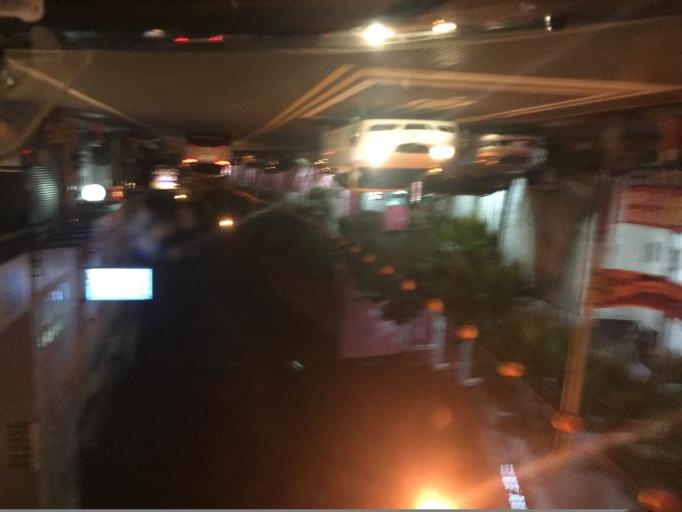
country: TW
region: Taiwan
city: Daxi
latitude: 24.9426
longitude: 121.2114
